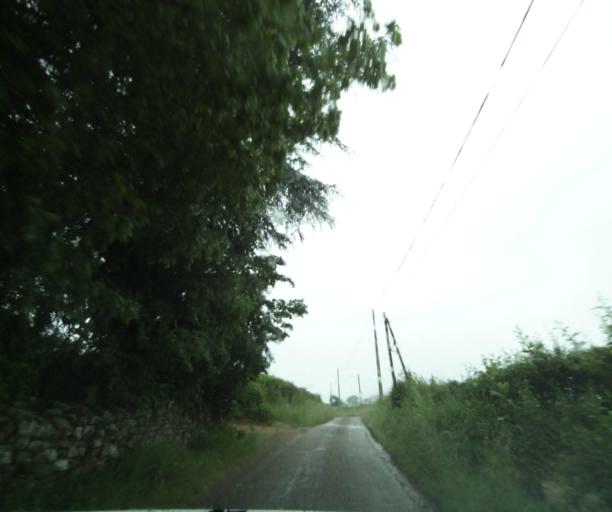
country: FR
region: Bourgogne
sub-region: Departement de Saone-et-Loire
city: Charolles
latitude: 46.3727
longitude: 4.3492
